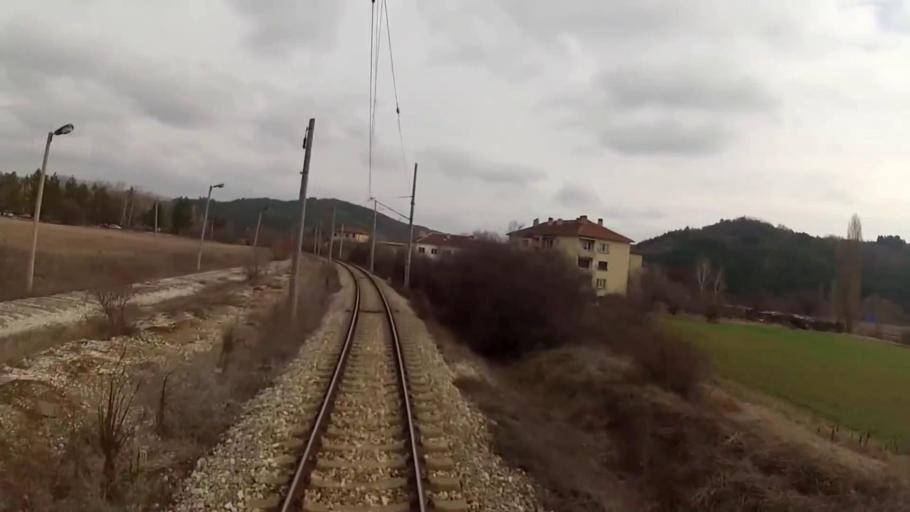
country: BG
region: Sofiya
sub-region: Obshtina Gorna Malina
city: Gorna Malina
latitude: 42.7138
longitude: 23.7016
